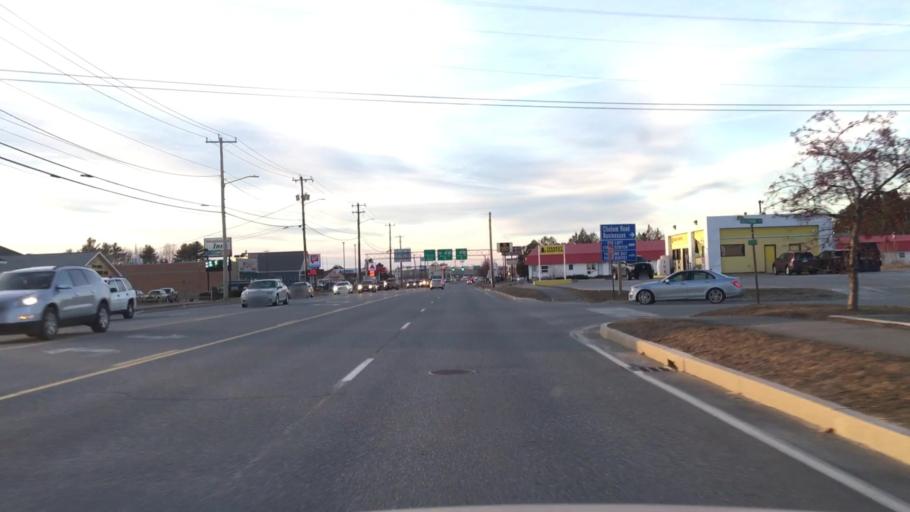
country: US
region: Maine
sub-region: Penobscot County
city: Brewer
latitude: 44.7824
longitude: -68.7472
